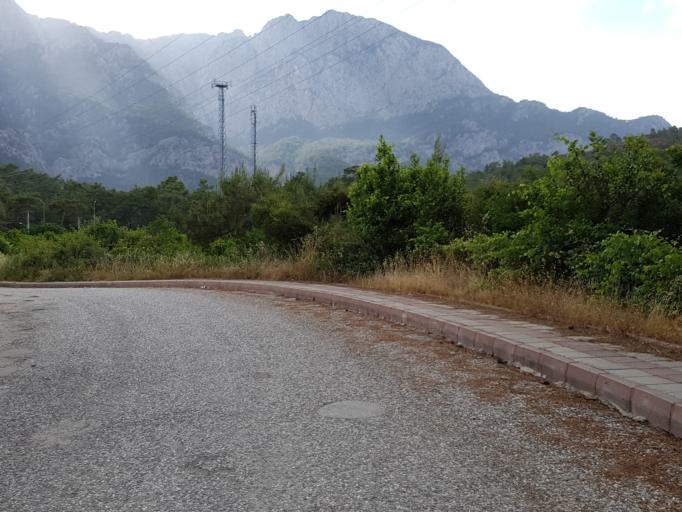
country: TR
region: Antalya
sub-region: Kemer
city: Goeynuek
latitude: 36.6439
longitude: 30.5507
